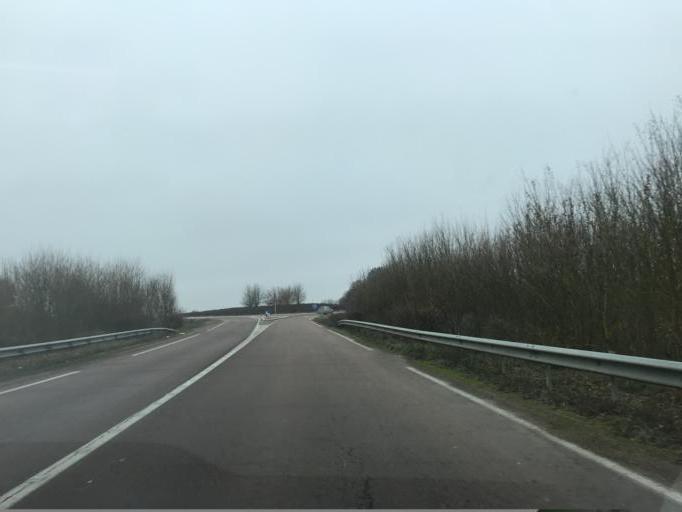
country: FR
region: Bourgogne
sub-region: Departement de l'Yonne
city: Avallon
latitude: 47.4997
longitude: 3.9295
